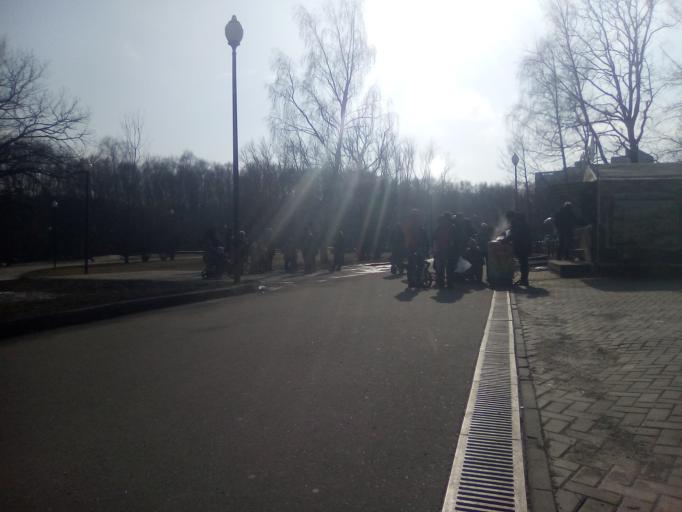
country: RU
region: Moscow
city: Tyoply Stan
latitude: 55.6371
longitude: 37.4917
